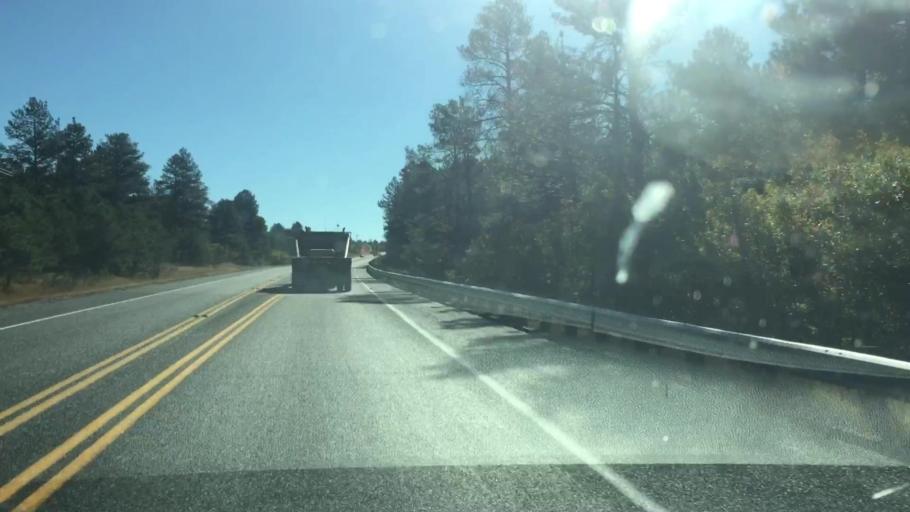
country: US
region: Colorado
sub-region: Elbert County
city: Ponderosa Park
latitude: 39.3773
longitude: -104.6969
